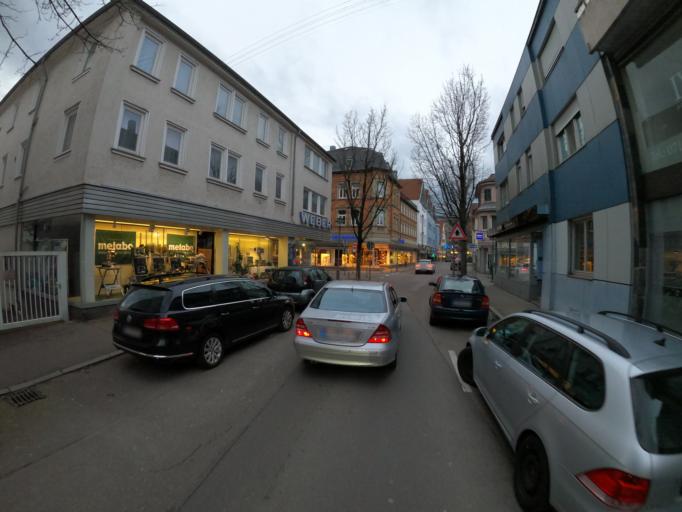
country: DE
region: Baden-Wuerttemberg
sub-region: Regierungsbezirk Stuttgart
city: Goeppingen
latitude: 48.7022
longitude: 9.6512
